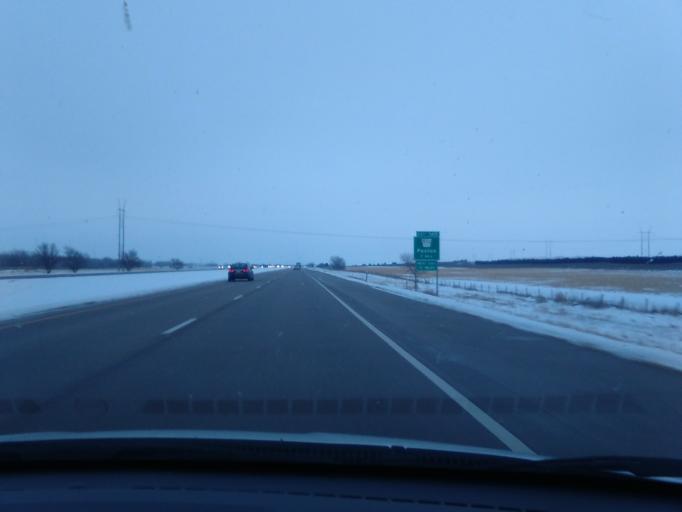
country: US
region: Nebraska
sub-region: Lincoln County
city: Sutherland
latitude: 41.1082
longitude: -101.3800
